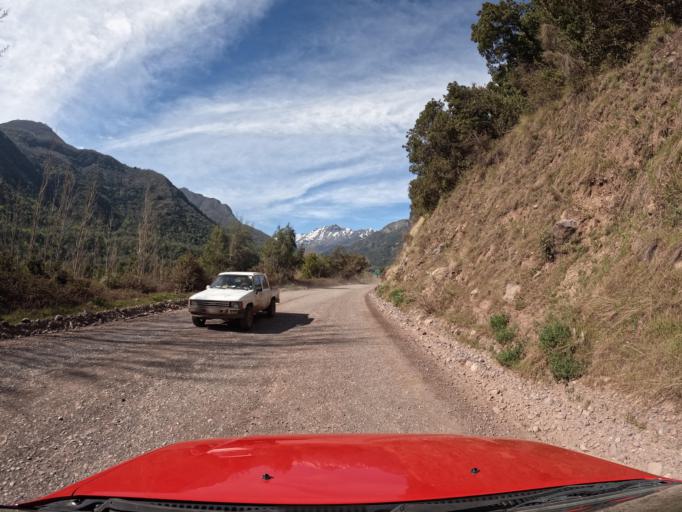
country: CL
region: O'Higgins
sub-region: Provincia de Colchagua
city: Chimbarongo
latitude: -34.9999
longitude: -70.7853
